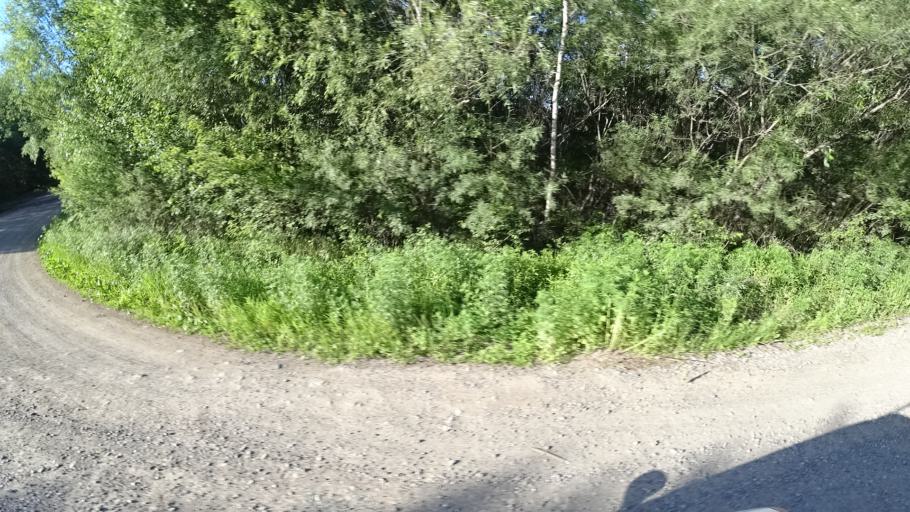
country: RU
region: Khabarovsk Krai
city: Khor
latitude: 47.8442
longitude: 134.9495
